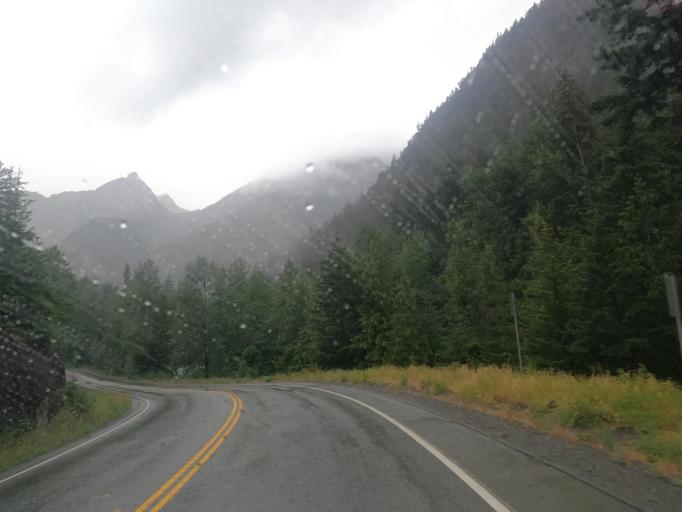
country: CA
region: British Columbia
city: Lillooet
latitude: 50.5356
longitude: -122.1428
